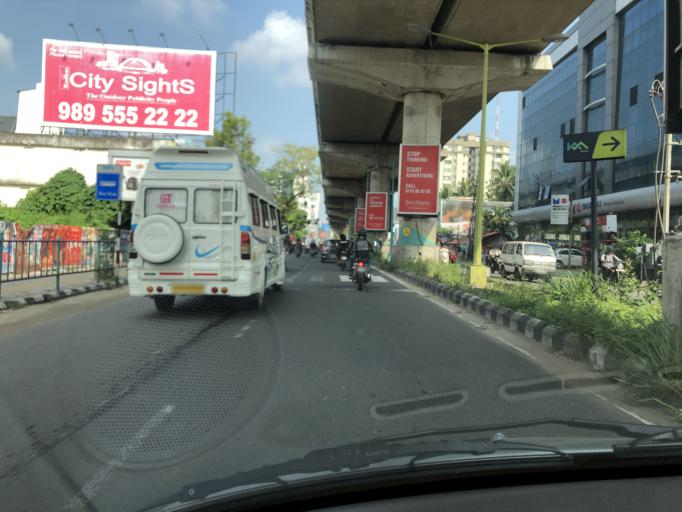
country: IN
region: Kerala
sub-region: Ernakulam
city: Elur
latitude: 10.0089
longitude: 76.3039
